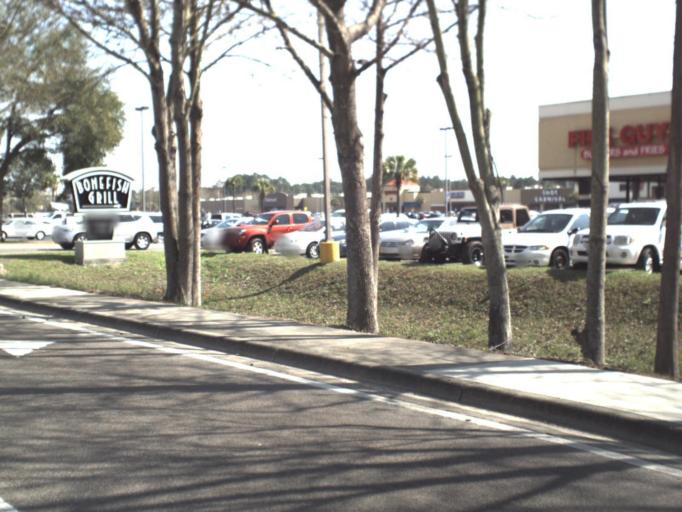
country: US
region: Florida
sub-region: Bay County
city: Pretty Bayou
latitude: 30.1897
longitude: -85.6713
